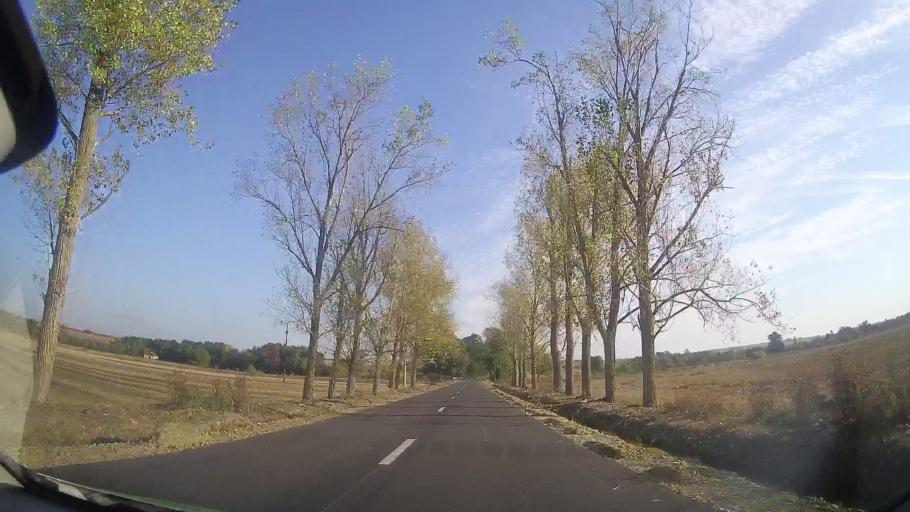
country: RO
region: Timis
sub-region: Comuna Masloc
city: Masloc
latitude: 45.9730
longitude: 21.4951
